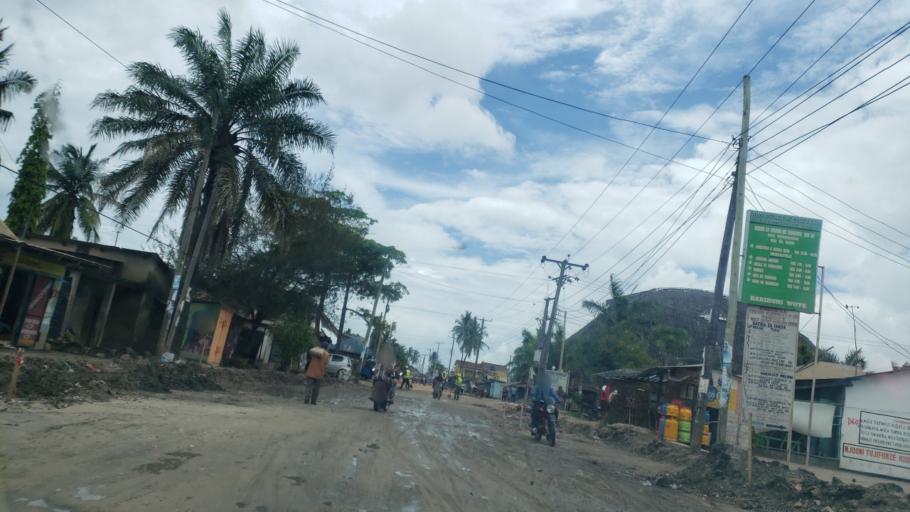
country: TZ
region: Dar es Salaam
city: Magomeni
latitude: -6.8065
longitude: 39.2291
